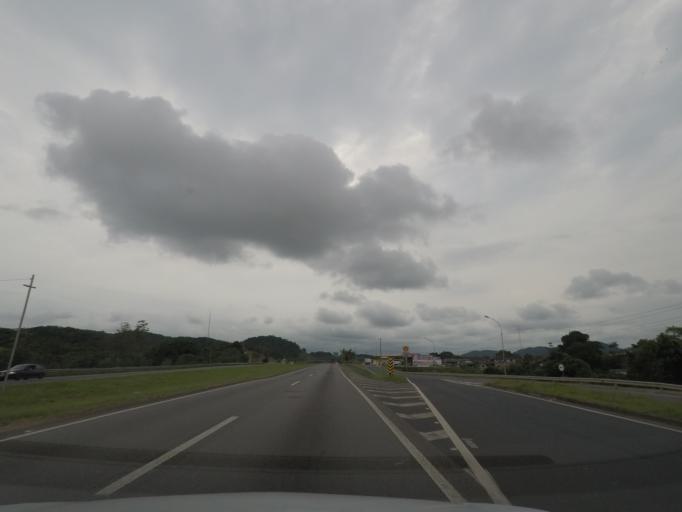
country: BR
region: Sao Paulo
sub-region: Juquia
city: Juquia
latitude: -24.3306
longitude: -47.6276
